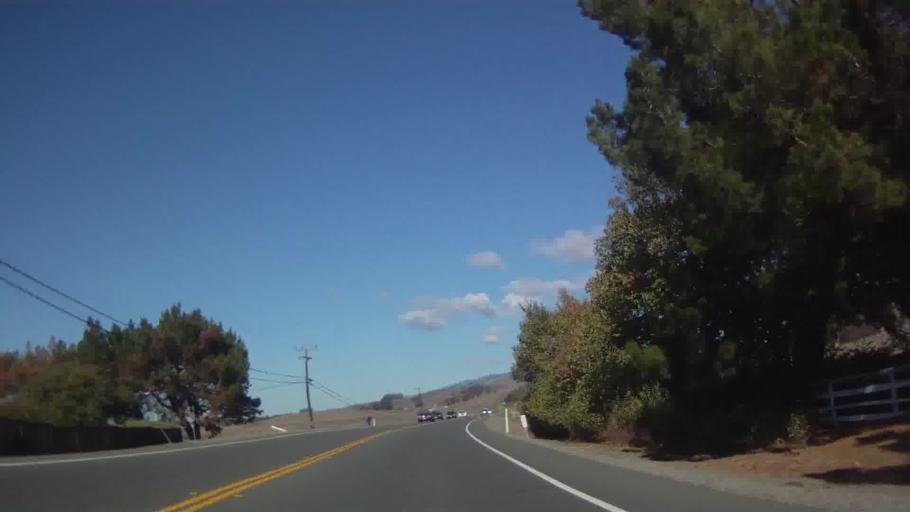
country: US
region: California
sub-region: Sonoma County
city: Temelec
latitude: 38.1986
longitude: -122.5466
